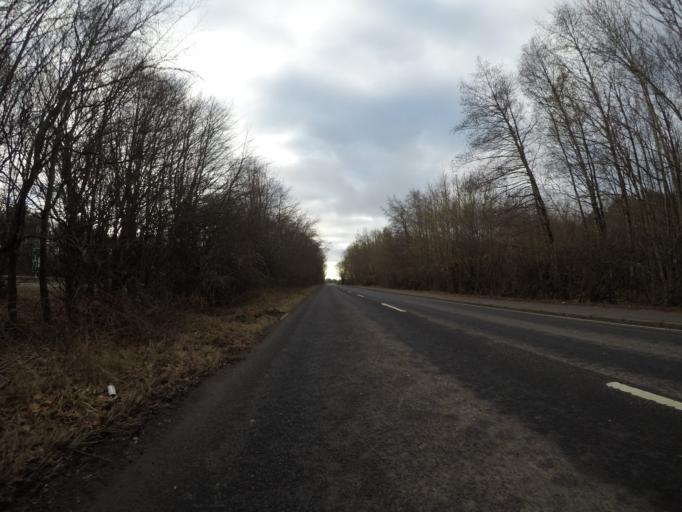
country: GB
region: Scotland
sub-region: North Ayrshire
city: Dreghorn
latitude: 55.5795
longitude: -4.6435
